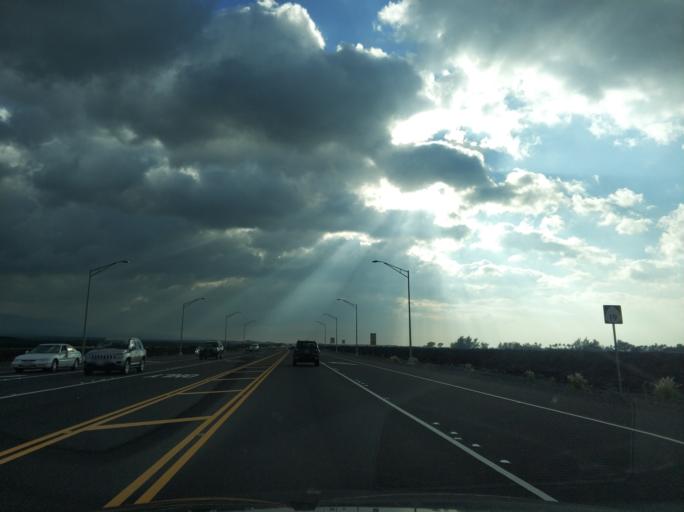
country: US
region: Hawaii
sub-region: Hawaii County
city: Waikoloa Village
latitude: 19.9216
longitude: -155.8611
